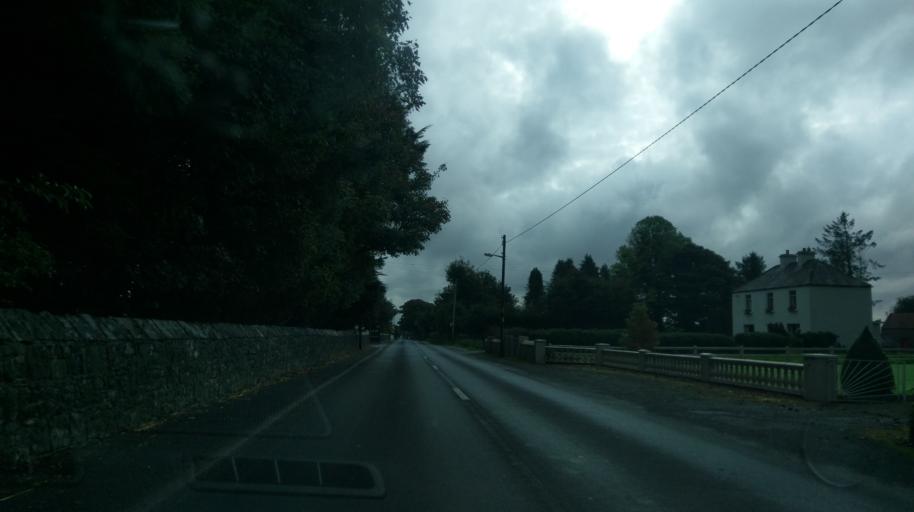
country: IE
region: Connaught
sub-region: County Galway
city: Loughrea
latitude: 53.4612
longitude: -8.4853
